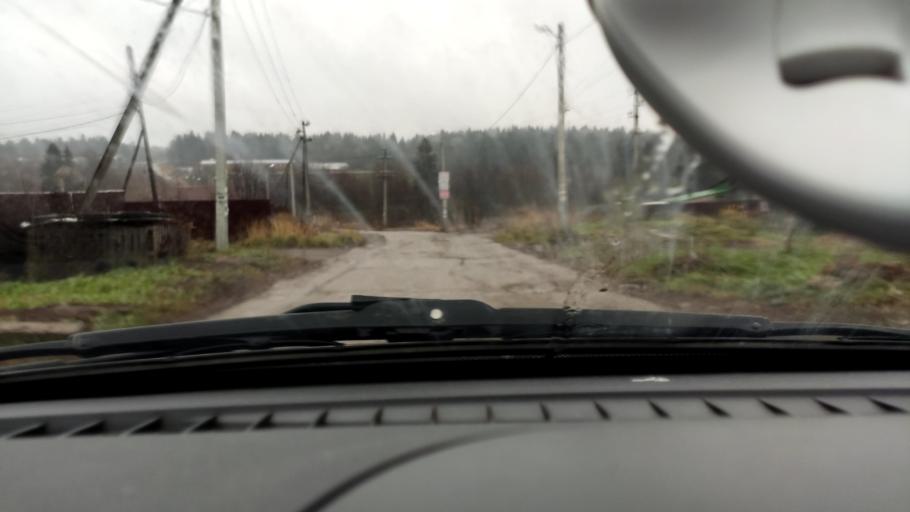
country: RU
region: Perm
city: Perm
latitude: 58.0366
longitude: 56.4088
